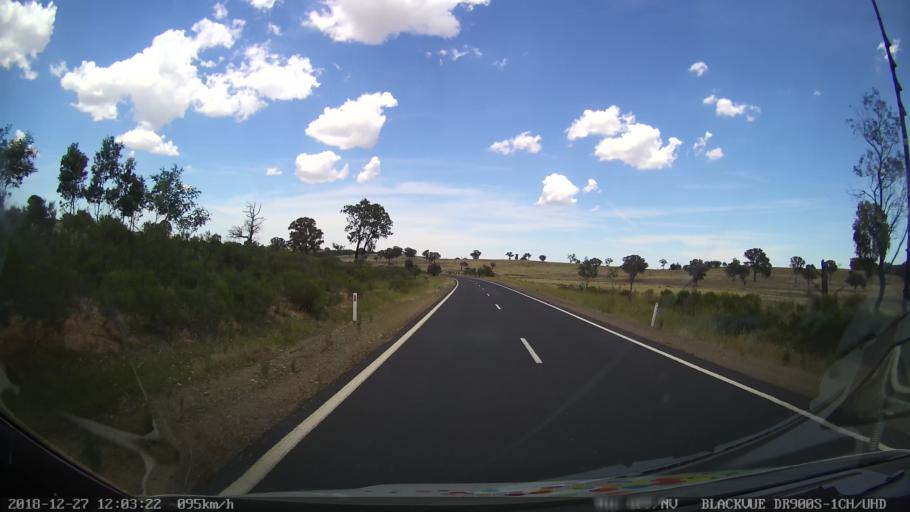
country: AU
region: New South Wales
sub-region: Blayney
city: Blayney
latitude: -33.7845
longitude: 149.3593
